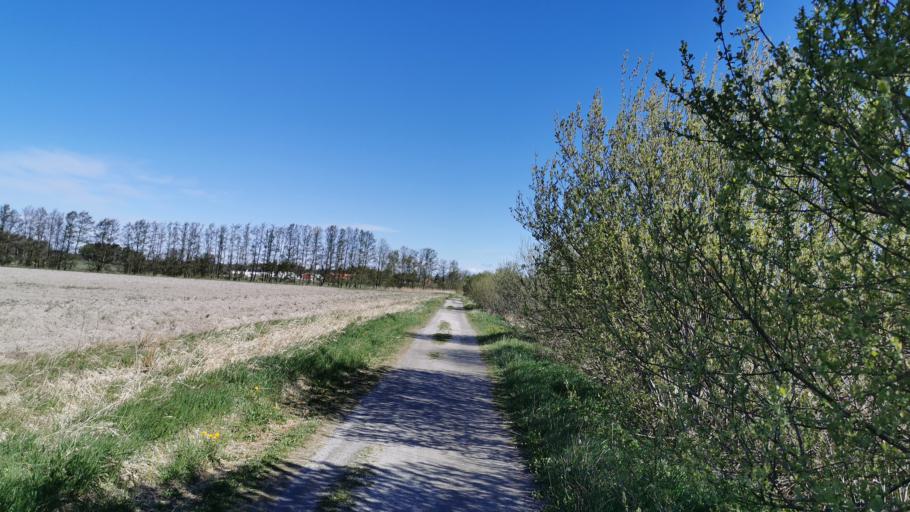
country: SE
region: OErebro
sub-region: Orebro Kommun
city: Orebro
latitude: 59.3065
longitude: 15.2166
